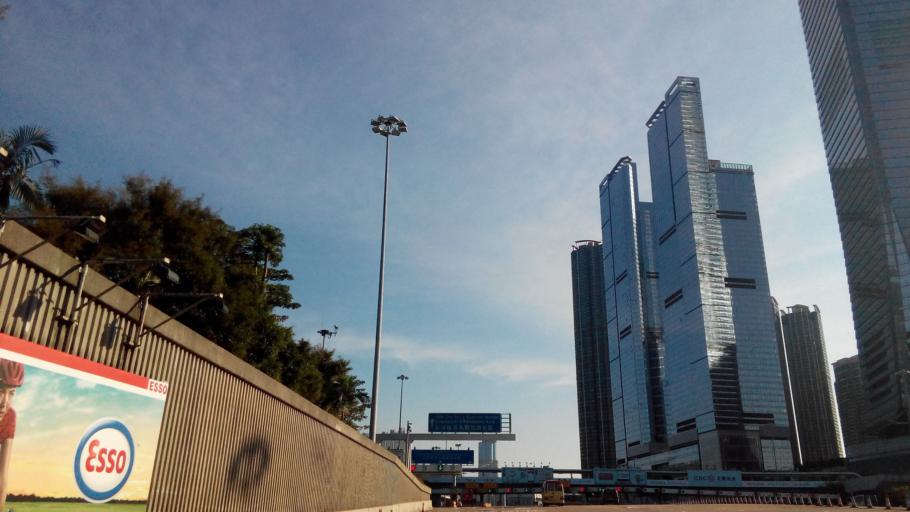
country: HK
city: Hong Kong
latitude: 22.3020
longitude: 114.1571
